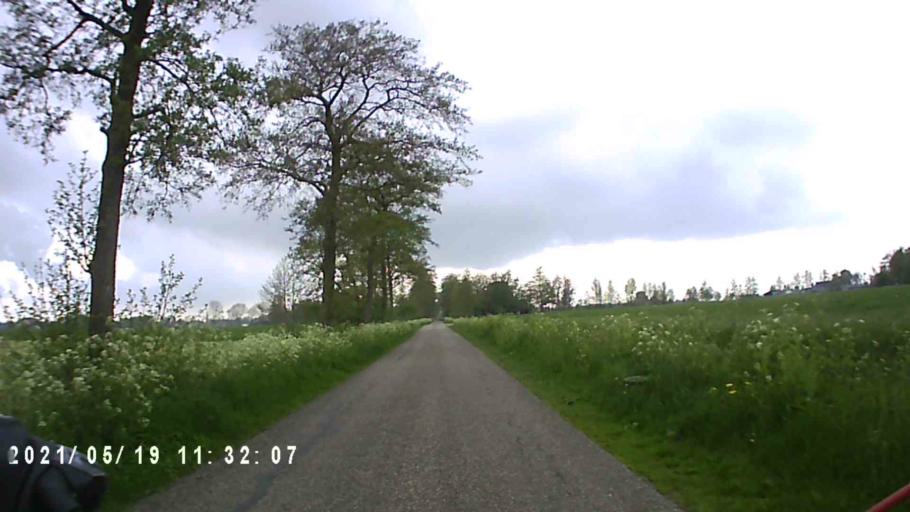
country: NL
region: Friesland
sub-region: Gemeente Kollumerland en Nieuwkruisland
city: Kollum
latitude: 53.2758
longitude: 6.1715
